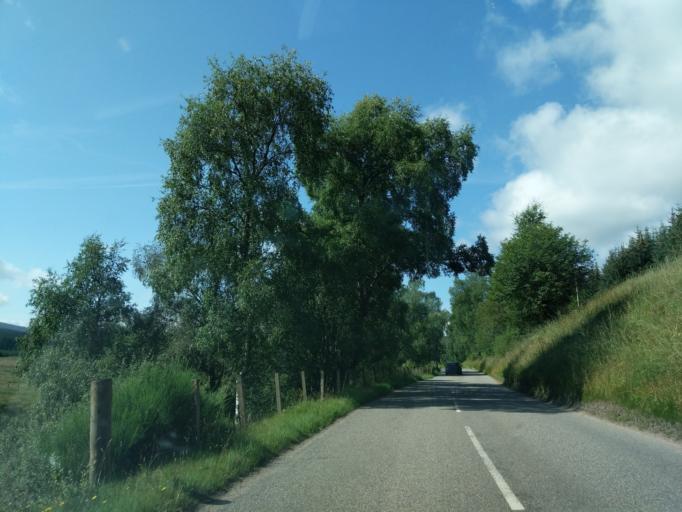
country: GB
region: Scotland
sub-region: Moray
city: Dufftown
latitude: 57.3708
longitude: -3.2542
